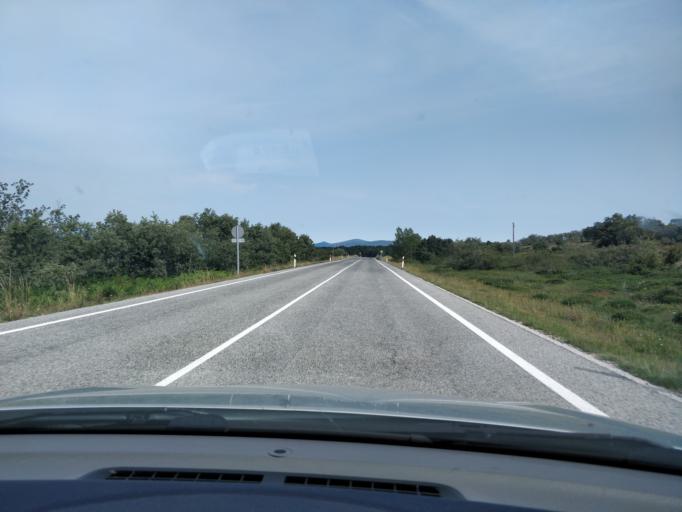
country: ES
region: Cantabria
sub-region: Provincia de Cantabria
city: San Martin de Elines
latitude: 42.9482
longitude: -3.7550
